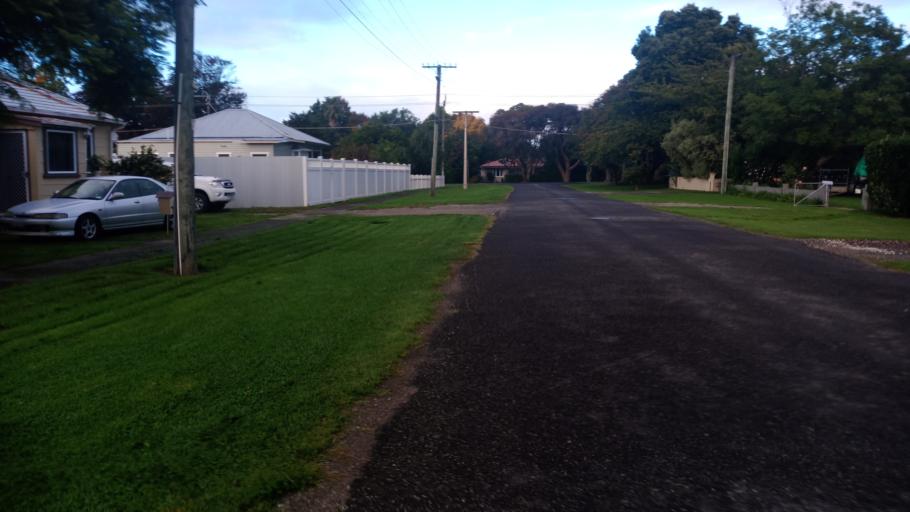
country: NZ
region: Gisborne
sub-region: Gisborne District
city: Gisborne
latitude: -38.6507
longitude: 178.0158
